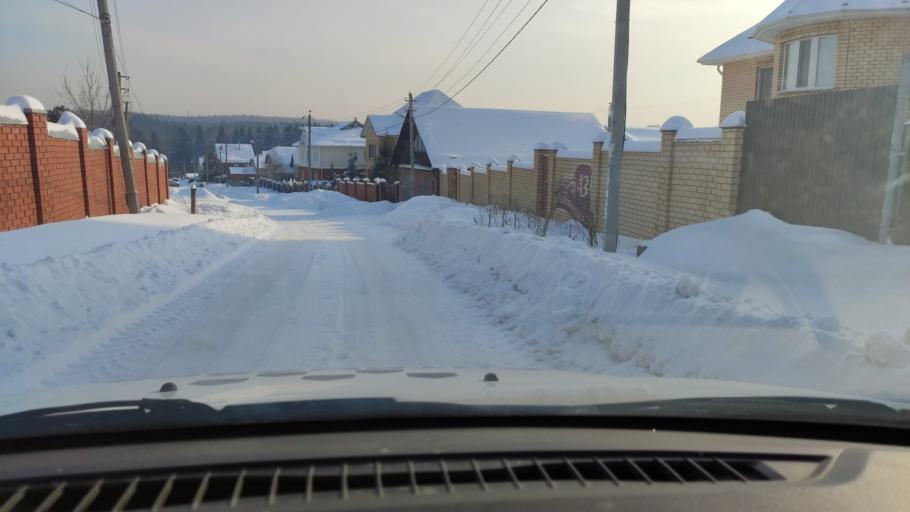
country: RU
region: Perm
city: Perm
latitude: 58.0363
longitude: 56.3927
